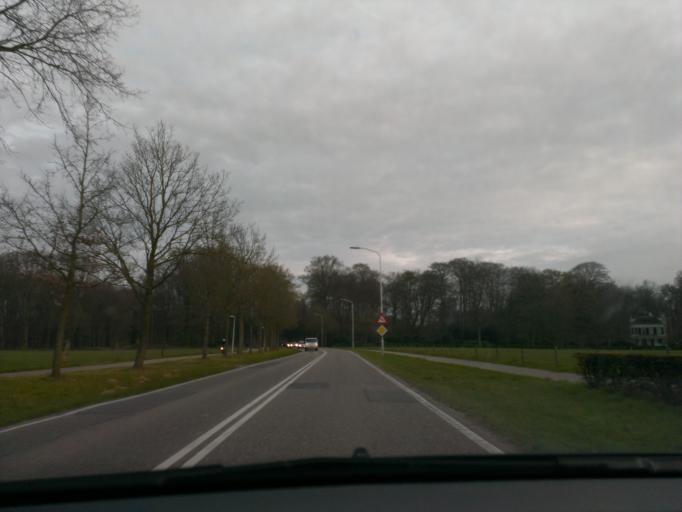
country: NL
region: Gelderland
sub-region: Gemeente Voorst
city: Twello
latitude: 52.2182
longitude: 6.1151
